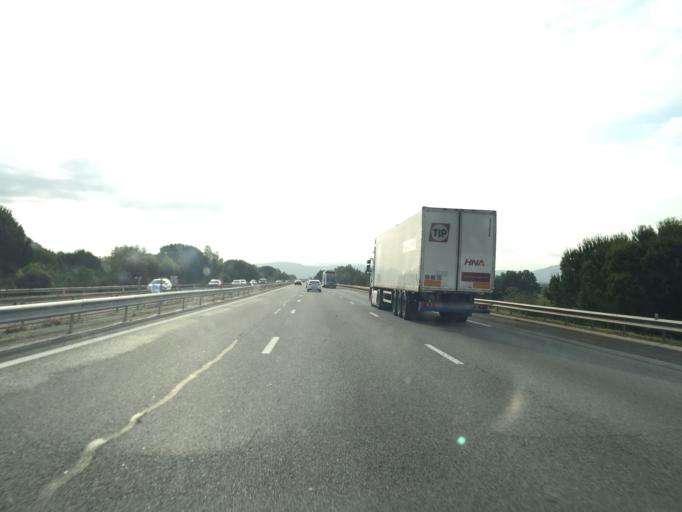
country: FR
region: Provence-Alpes-Cote d'Azur
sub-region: Departement du Var
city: Le Cannet-des-Maures
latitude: 43.4020
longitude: 6.3860
